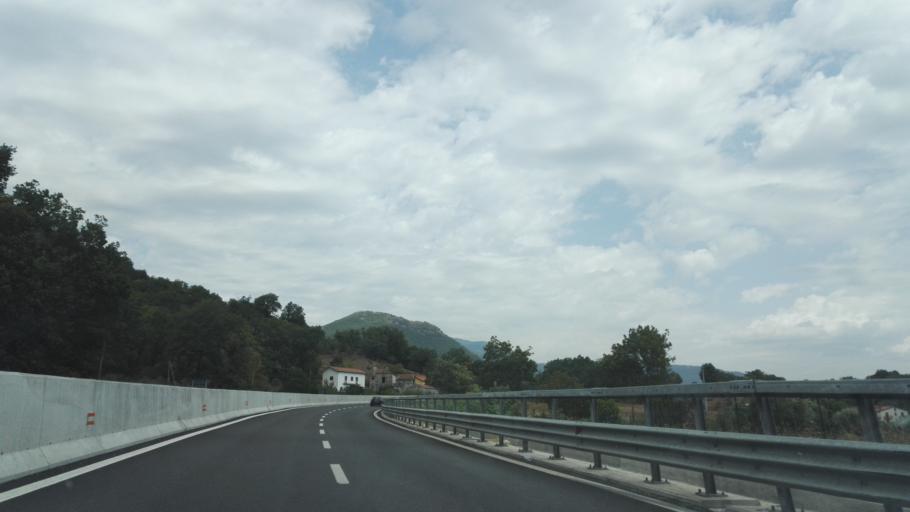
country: IT
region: Calabria
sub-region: Provincia di Cosenza
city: Laino Borgo
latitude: 39.9676
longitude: 15.9326
